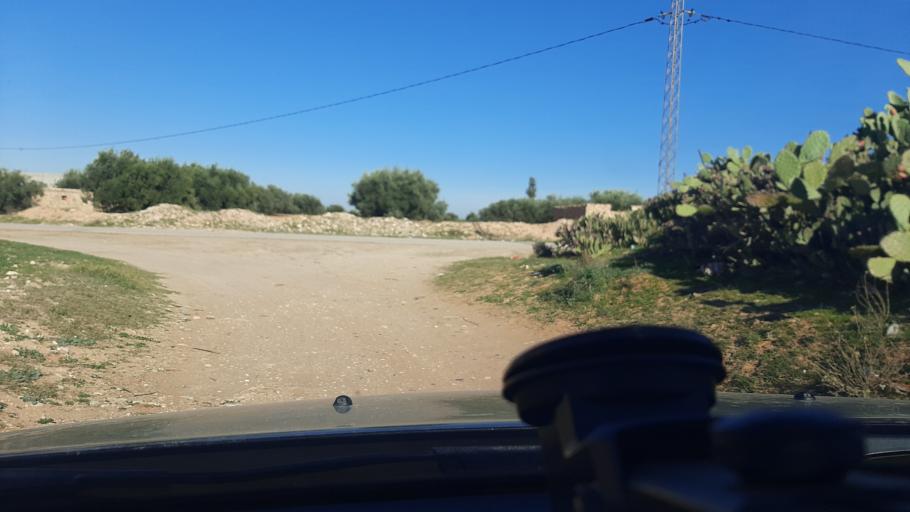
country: TN
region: Safaqis
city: Bi'r `Ali Bin Khalifah
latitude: 35.0072
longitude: 10.0900
